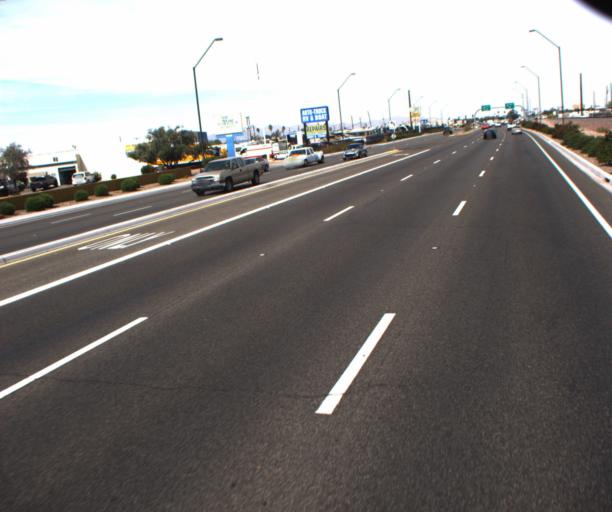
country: US
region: Arizona
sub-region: Maricopa County
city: Peoria
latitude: 33.5916
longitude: -112.2514
